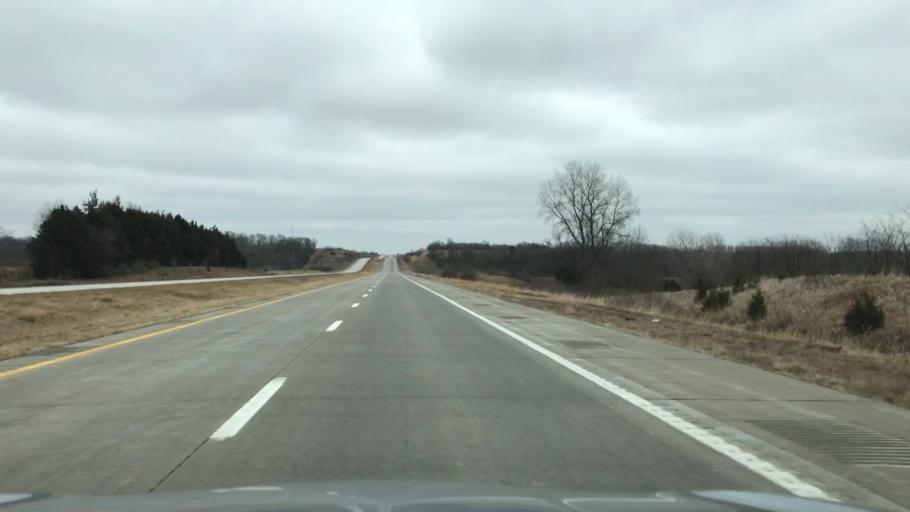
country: US
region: Missouri
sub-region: Caldwell County
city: Hamilton
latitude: 39.7350
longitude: -93.8288
